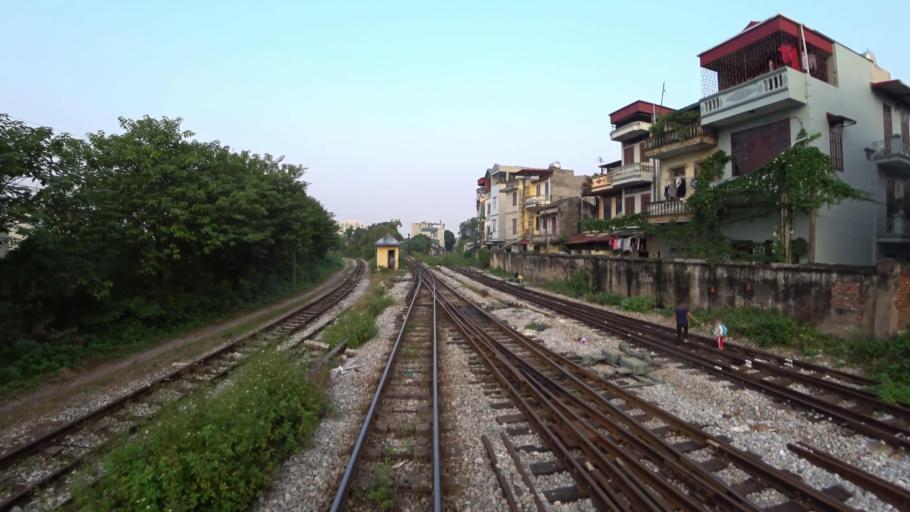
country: VN
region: Ha Noi
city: Trau Quy
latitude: 21.0682
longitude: 105.8995
